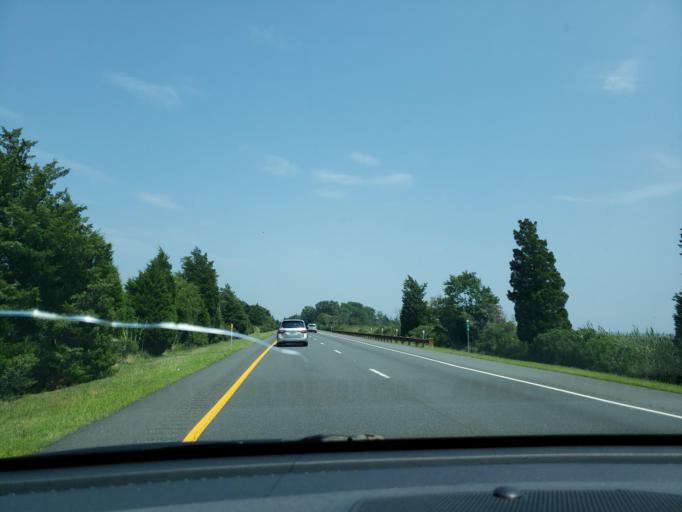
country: US
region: New Jersey
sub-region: Cape May County
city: Sea Isle City
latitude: 39.1500
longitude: -74.7523
